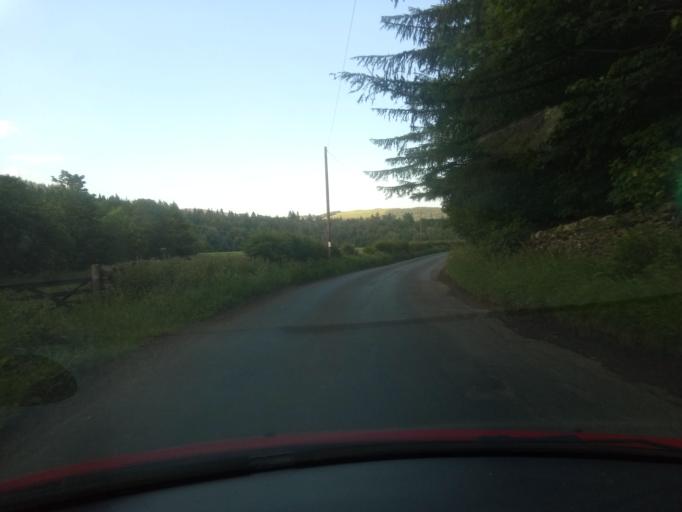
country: GB
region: Scotland
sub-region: The Scottish Borders
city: Selkirk
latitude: 55.5293
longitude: -2.9195
